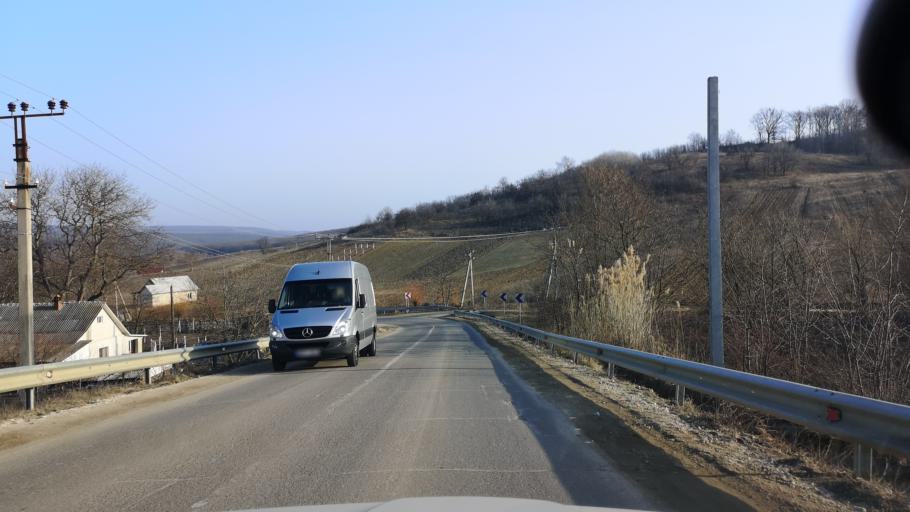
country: MD
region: Stinga Nistrului
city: Bucovat
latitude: 47.1084
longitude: 28.5048
